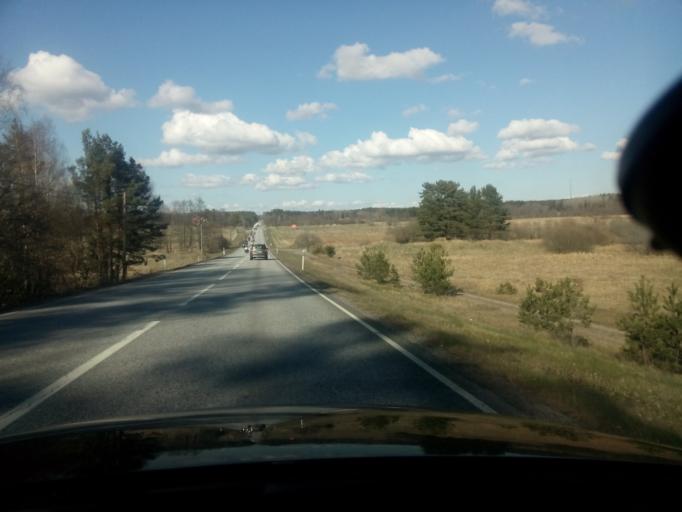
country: SE
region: Soedermanland
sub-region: Strangnas Kommun
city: Strangnas
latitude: 59.3043
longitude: 16.9862
